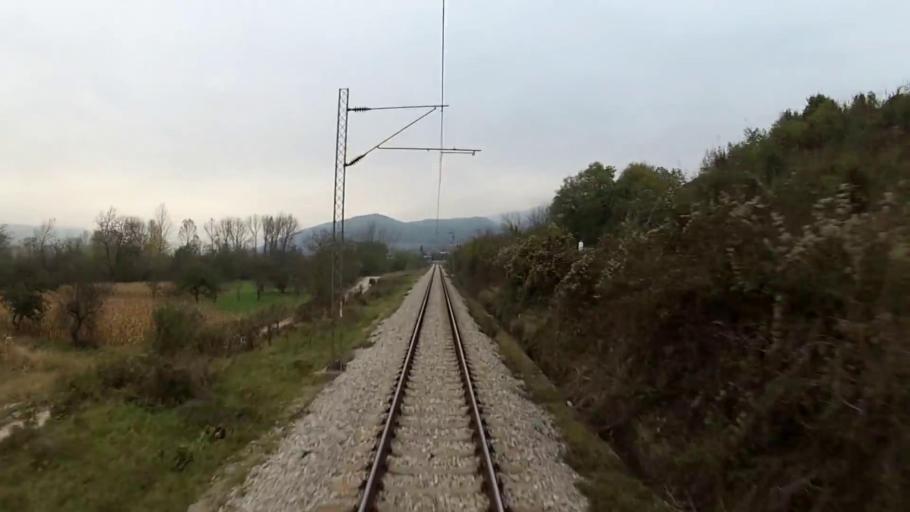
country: RS
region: Central Serbia
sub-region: Pirotski Okrug
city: Dimitrovgrad
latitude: 43.0062
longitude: 22.8061
